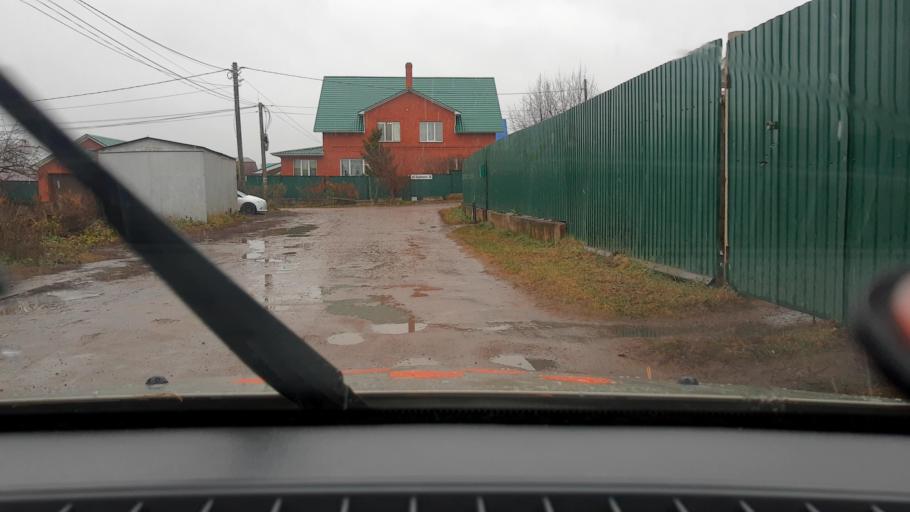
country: RU
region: Bashkortostan
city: Ufa
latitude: 54.6148
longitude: 55.9387
